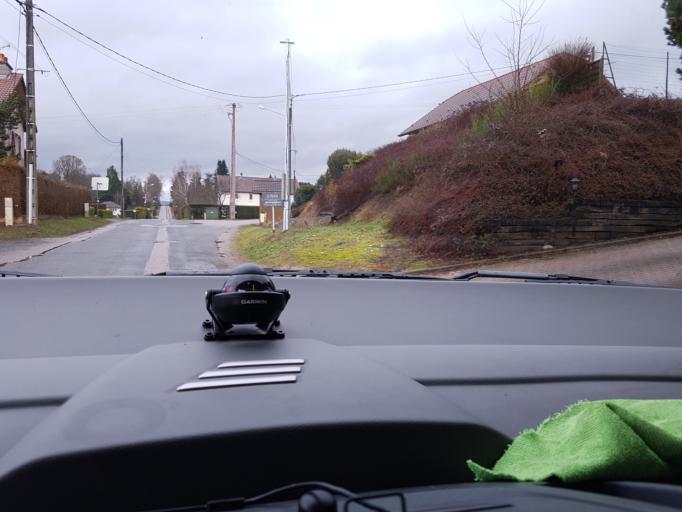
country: FR
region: Lorraine
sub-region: Departement des Vosges
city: Saint-Michel-sur-Meurthe
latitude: 48.3376
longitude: 6.8971
